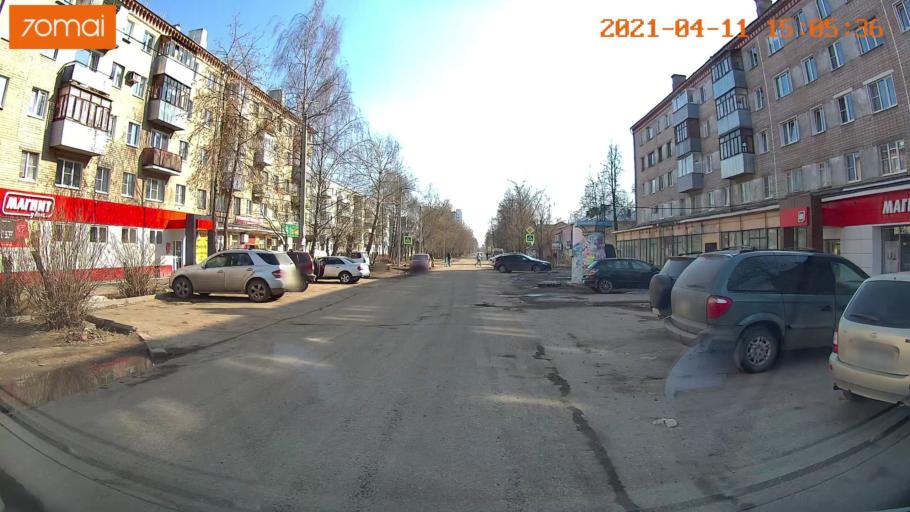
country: RU
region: Ivanovo
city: Bogorodskoye
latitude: 57.0220
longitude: 41.0150
